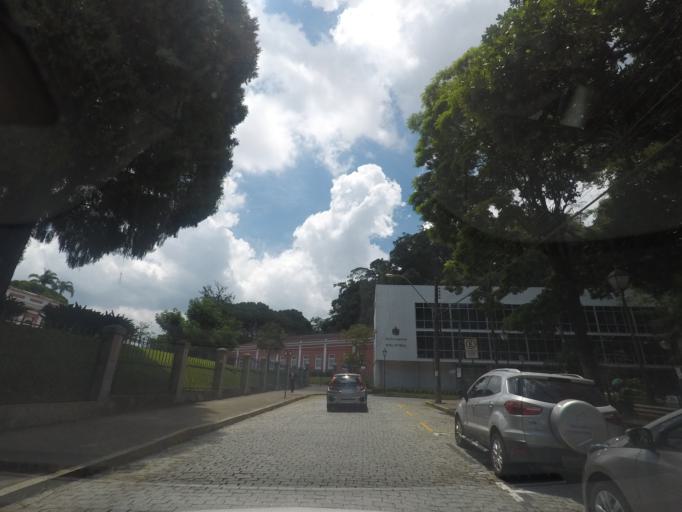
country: BR
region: Rio de Janeiro
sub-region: Petropolis
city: Petropolis
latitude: -22.5081
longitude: -43.1747
